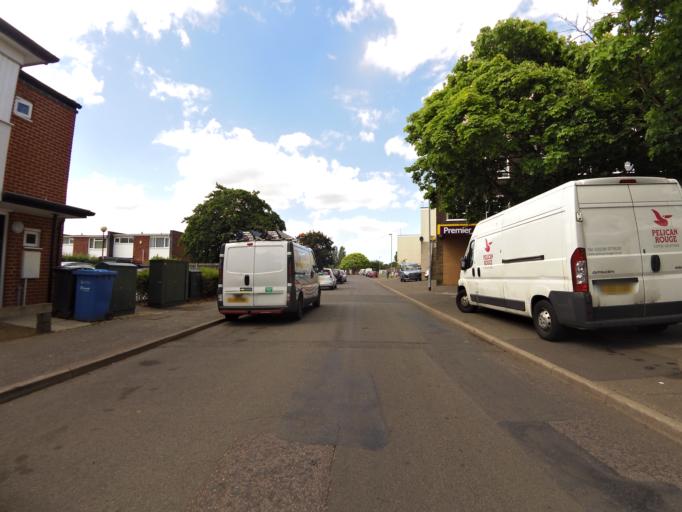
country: GB
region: England
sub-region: Norfolk
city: Norwich
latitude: 52.6521
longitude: 1.2697
